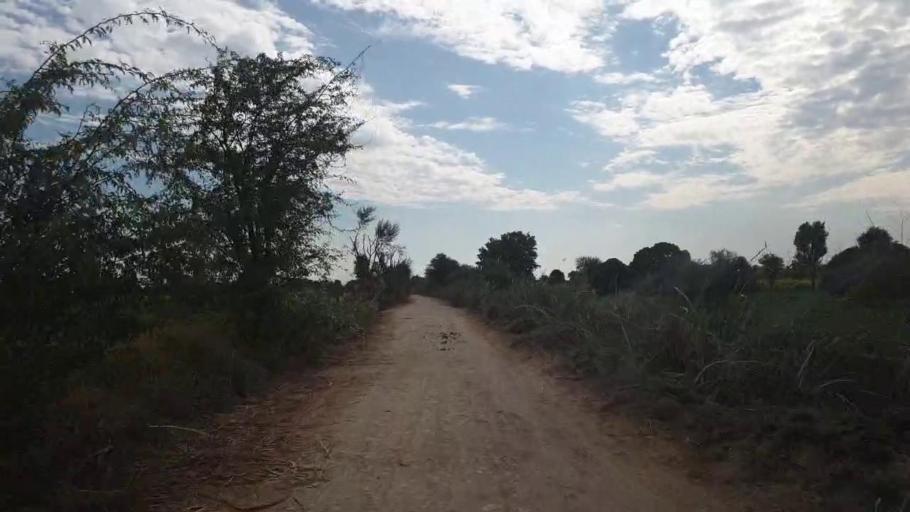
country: PK
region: Sindh
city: Jhol
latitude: 25.9894
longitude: 68.8991
